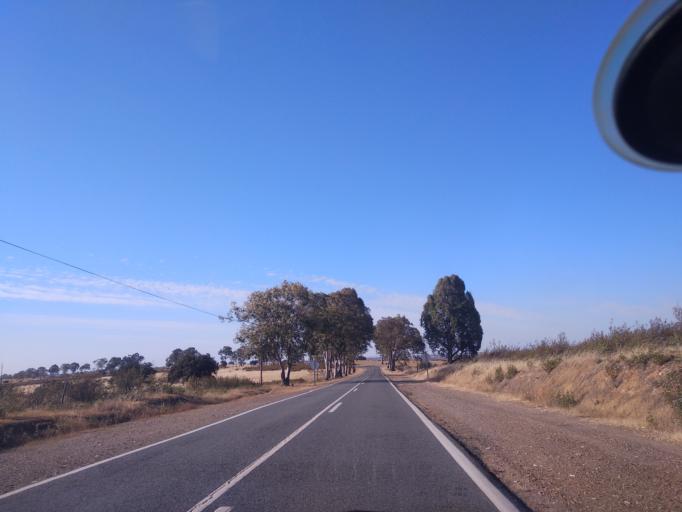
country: PT
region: Beja
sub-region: Almodovar
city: Almodovar
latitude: 37.4494
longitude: -7.9968
